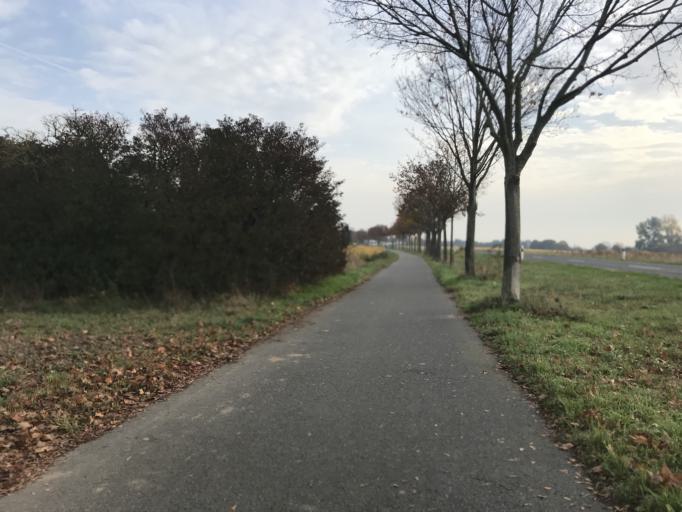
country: DE
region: Hesse
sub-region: Regierungsbezirk Darmstadt
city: Ginsheim-Gustavsburg
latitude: 49.9596
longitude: 8.3653
